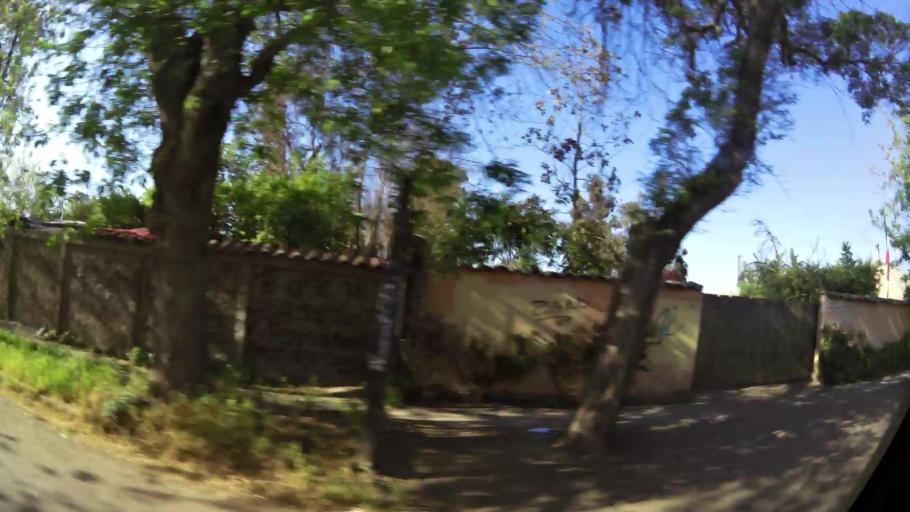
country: CL
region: Santiago Metropolitan
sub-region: Provincia de Talagante
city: Penaflor
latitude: -33.6083
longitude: -70.8625
